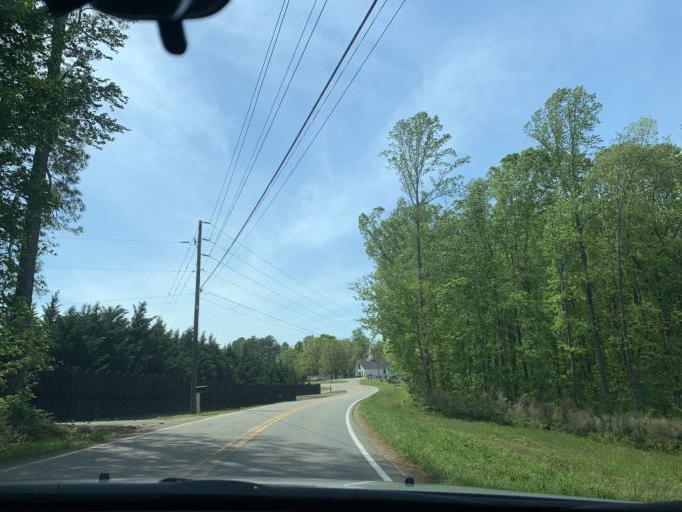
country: US
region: Georgia
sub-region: Forsyth County
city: Cumming
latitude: 34.2660
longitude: -84.1791
